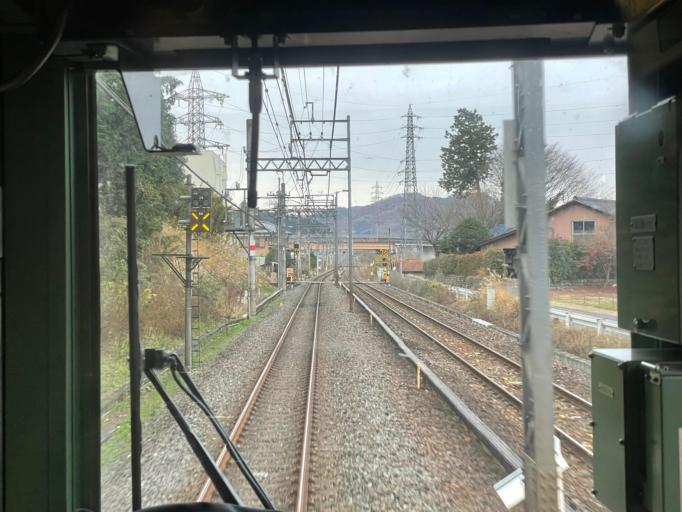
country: JP
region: Saitama
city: Ogawa
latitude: 36.0629
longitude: 139.2494
